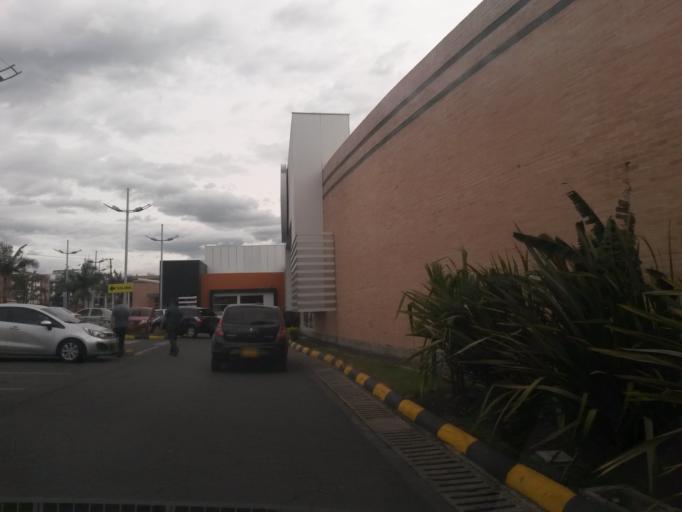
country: CO
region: Cauca
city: Popayan
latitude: 2.4590
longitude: -76.5941
